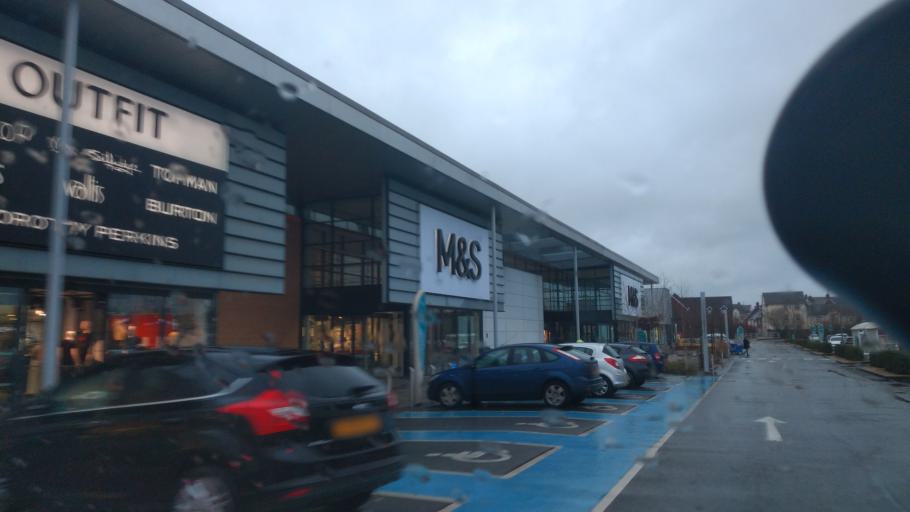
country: GB
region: England
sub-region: Borough of Swindon
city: Broad Blunsdon
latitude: 51.5978
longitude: -1.8076
